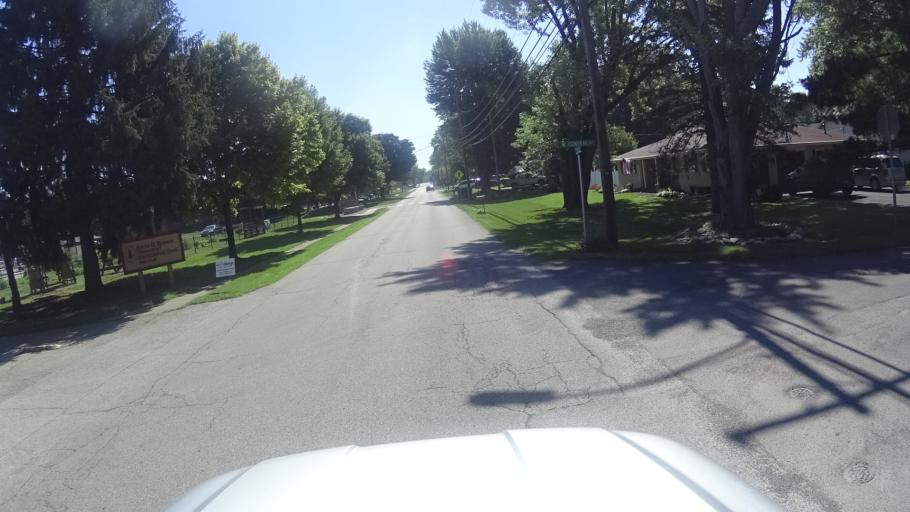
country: US
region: Indiana
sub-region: Madison County
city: Pendleton
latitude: 40.0037
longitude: -85.7371
